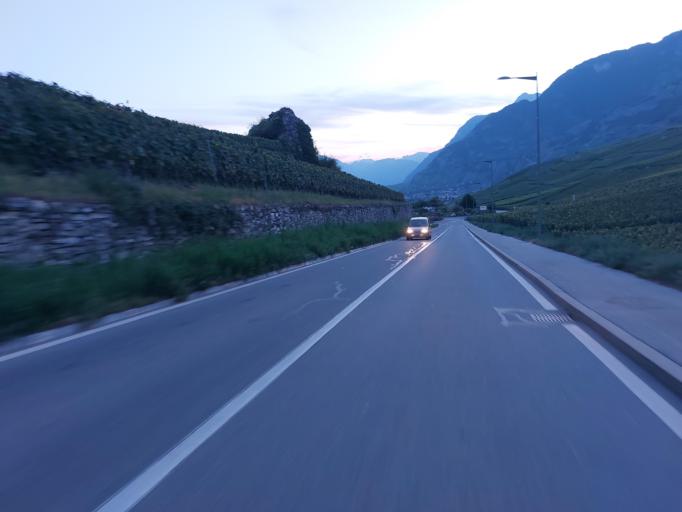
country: CH
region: Valais
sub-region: Conthey District
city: Conthey
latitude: 46.2339
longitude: 7.3040
